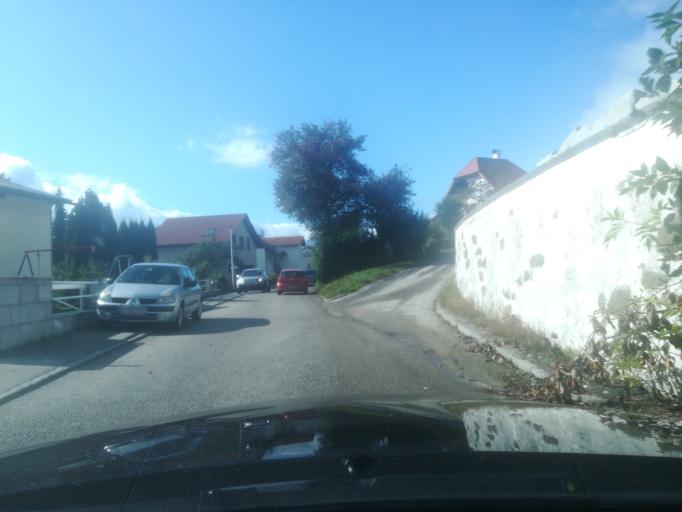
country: AT
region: Upper Austria
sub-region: Politischer Bezirk Urfahr-Umgebung
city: Eidenberg
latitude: 48.3585
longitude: 14.2613
